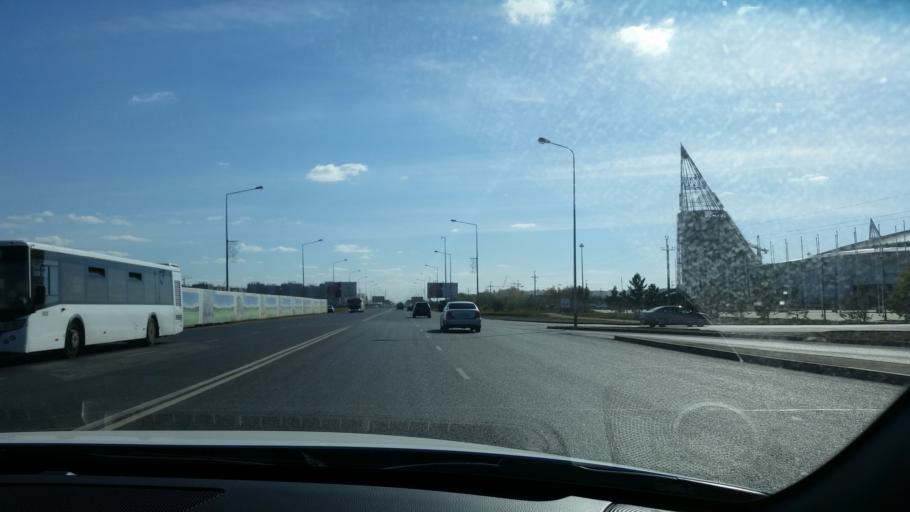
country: KZ
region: Astana Qalasy
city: Astana
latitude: 51.1065
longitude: 71.4087
